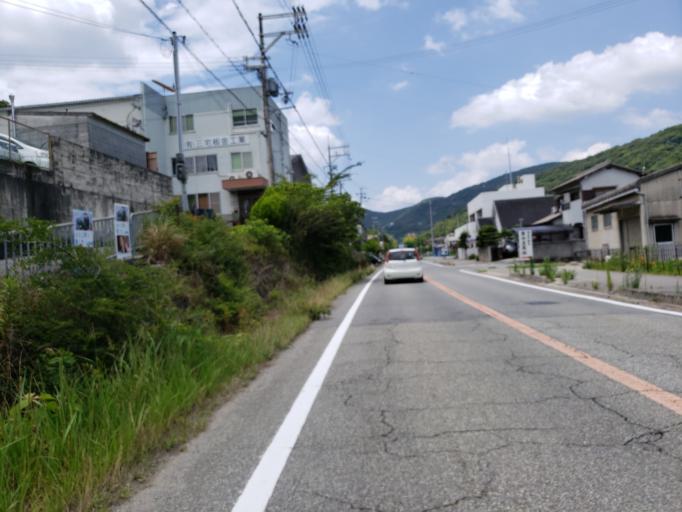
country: JP
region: Hyogo
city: Aioi
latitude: 34.7815
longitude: 134.5405
